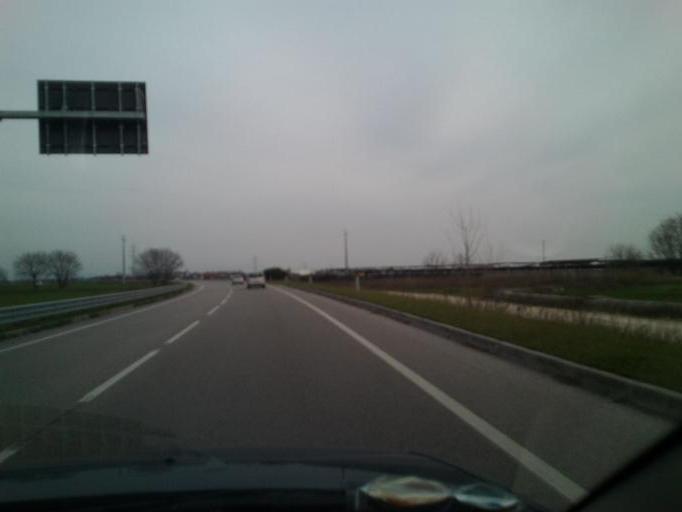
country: IT
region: Veneto
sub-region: Provincia di Verona
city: Povegliano Veronese
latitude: 45.3644
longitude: 10.8866
